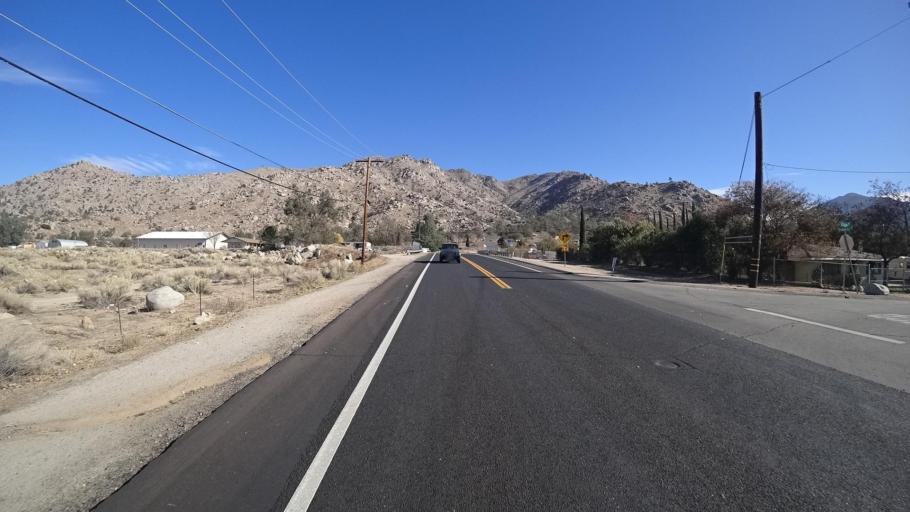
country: US
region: California
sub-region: Kern County
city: Lake Isabella
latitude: 35.6169
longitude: -118.4660
